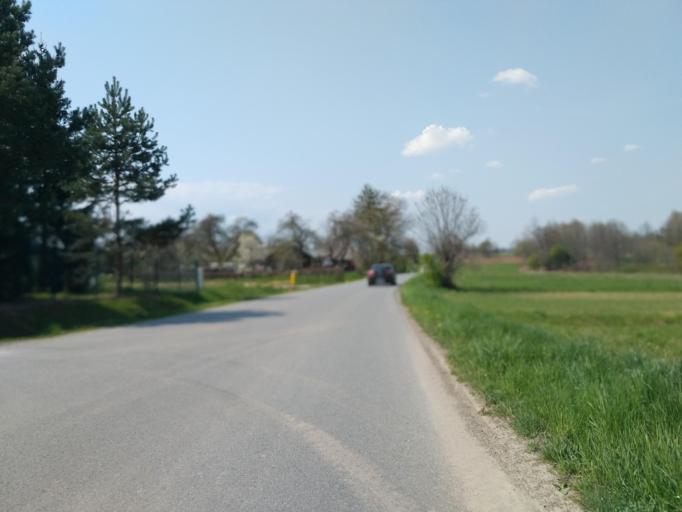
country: PL
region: Subcarpathian Voivodeship
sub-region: Powiat jasielski
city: Tarnowiec
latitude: 49.6688
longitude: 21.5930
